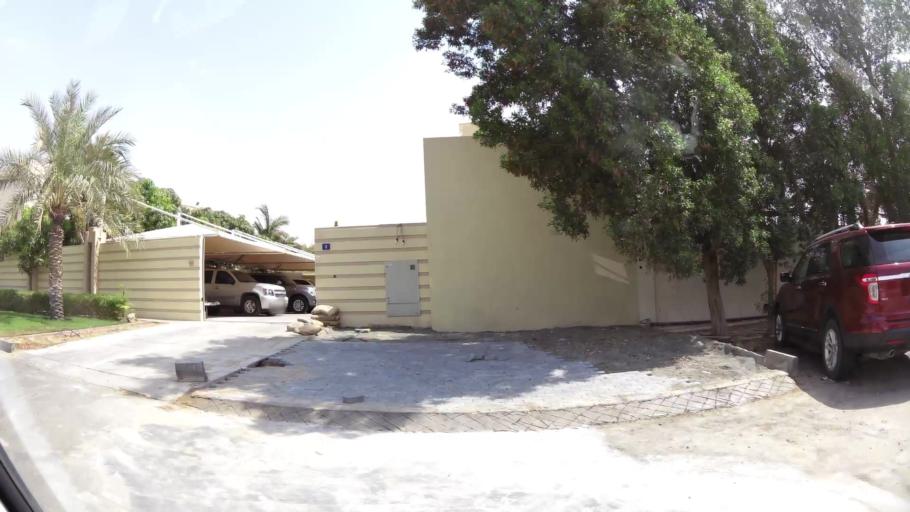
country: AE
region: Ash Shariqah
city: Sharjah
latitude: 25.2560
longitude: 55.4783
